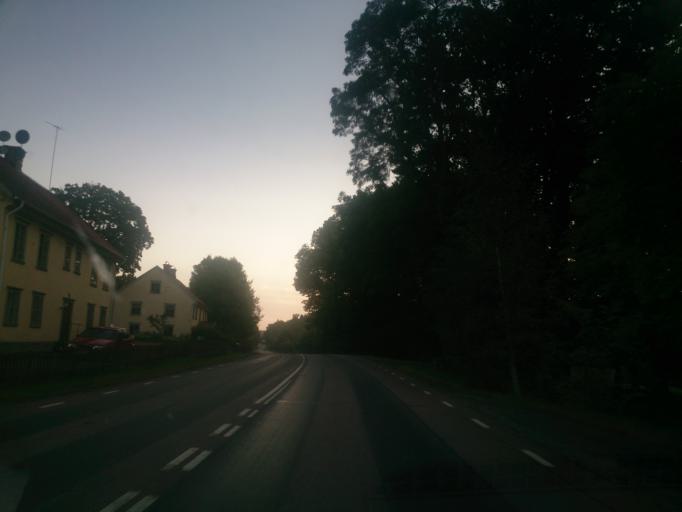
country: SE
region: Soedermanland
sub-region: Nykopings Kommun
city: Nykoping
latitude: 58.8195
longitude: 17.0919
